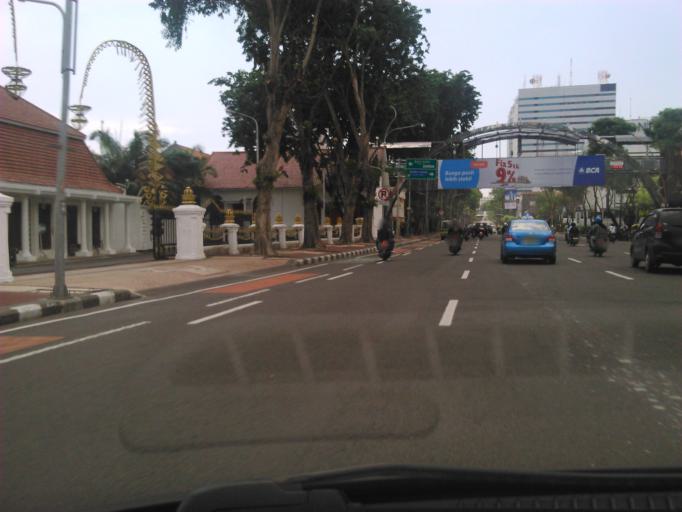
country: ID
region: East Java
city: Pacarkeling
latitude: -7.2636
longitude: 112.7434
